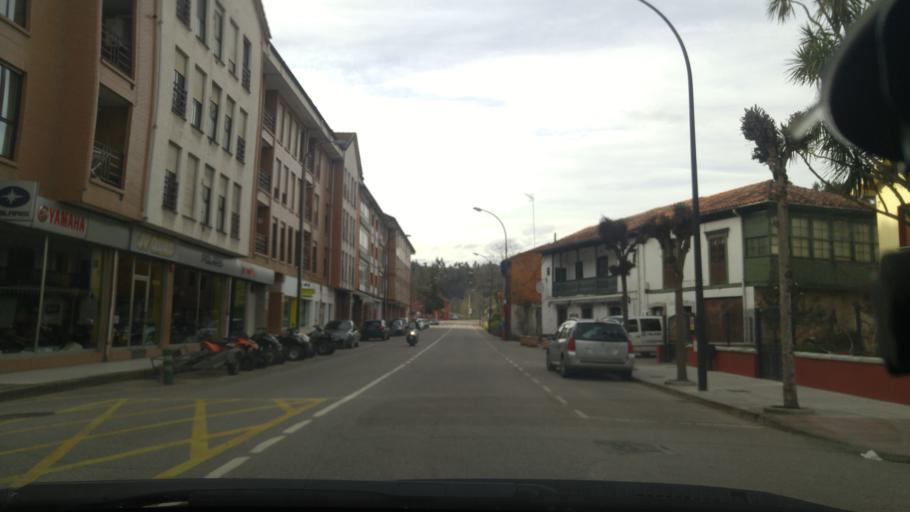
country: ES
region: Asturias
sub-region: Province of Asturias
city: Llanera
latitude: 43.4423
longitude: -5.8543
